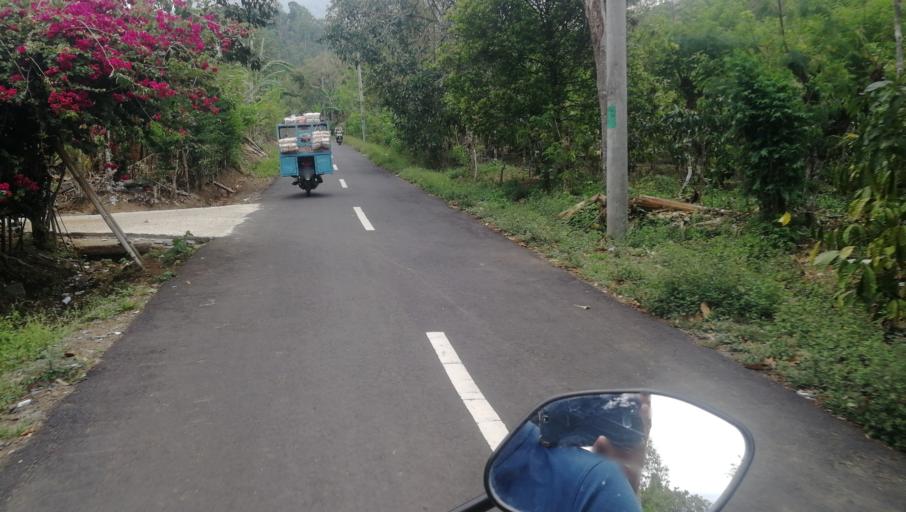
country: ID
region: Bali
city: Munduk
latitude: -8.3032
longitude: 115.0590
